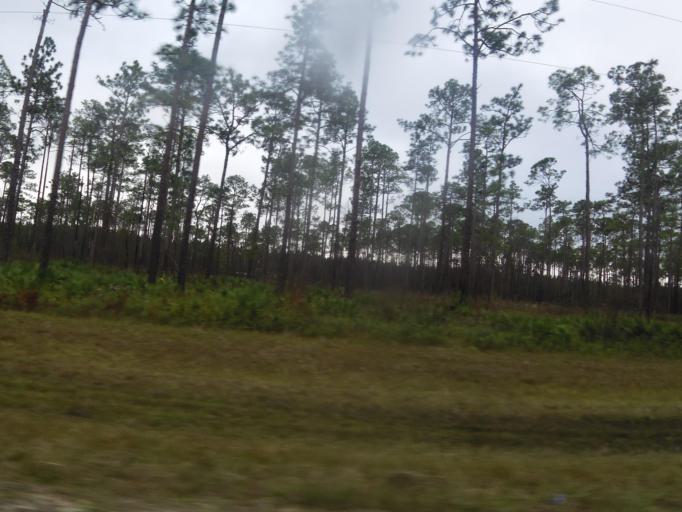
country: US
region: Georgia
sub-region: Charlton County
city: Folkston
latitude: 30.7403
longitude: -82.0751
